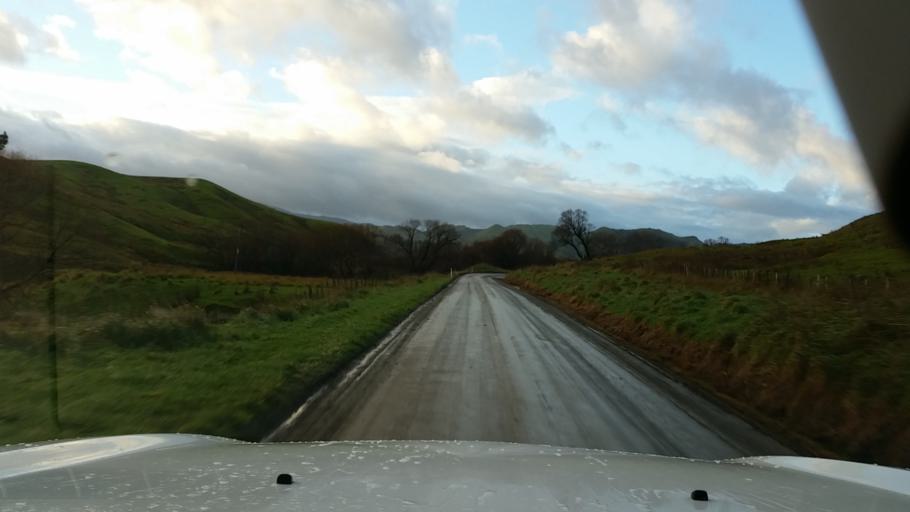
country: NZ
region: Wellington
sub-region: South Wairarapa District
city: Waipawa
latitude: -41.2917
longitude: 175.6423
